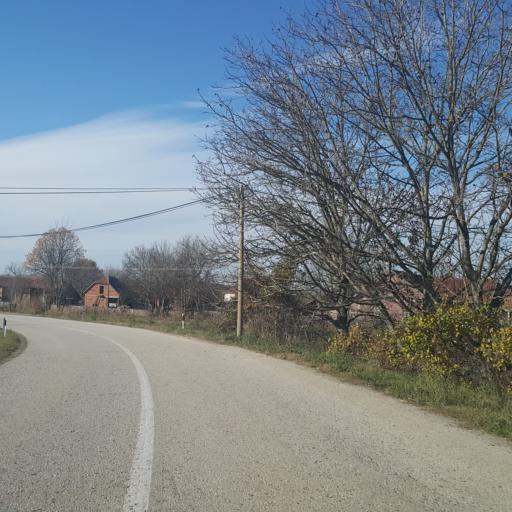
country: RS
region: Central Serbia
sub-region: Sumadijski Okrug
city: Topola
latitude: 44.2586
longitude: 20.8243
